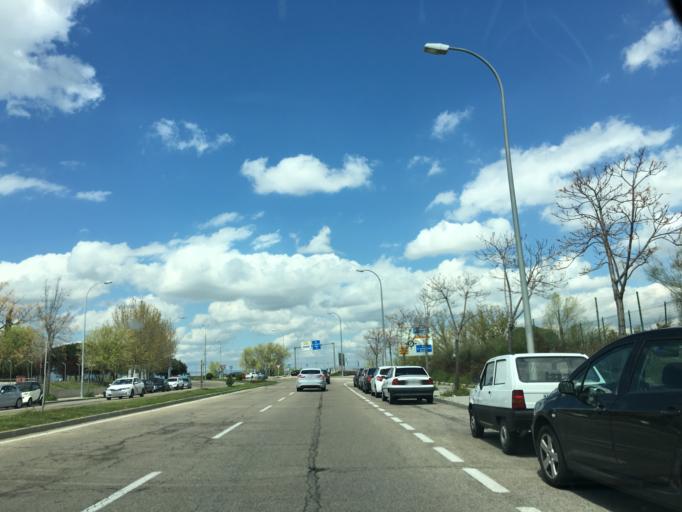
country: ES
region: Madrid
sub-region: Provincia de Madrid
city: Hortaleza
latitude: 40.4698
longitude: -3.6124
